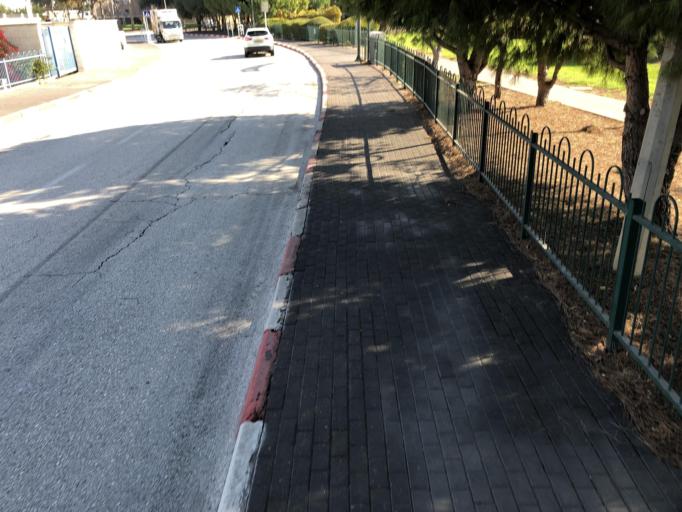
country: IL
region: Northern District
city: `Akko
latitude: 32.9218
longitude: 35.0928
